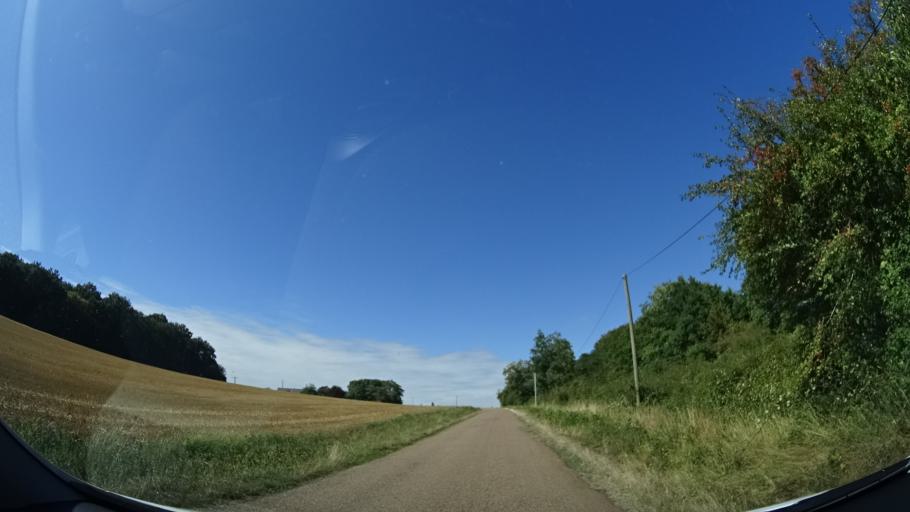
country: FR
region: Centre
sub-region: Departement du Loiret
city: Trigueres
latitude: 47.9521
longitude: 2.9827
